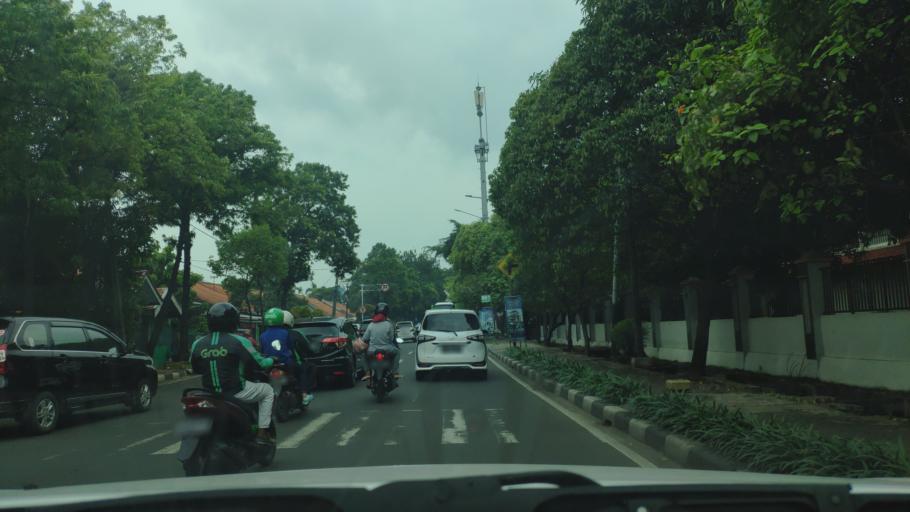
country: ID
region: Jakarta Raya
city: Jakarta
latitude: -6.1884
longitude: 106.7848
